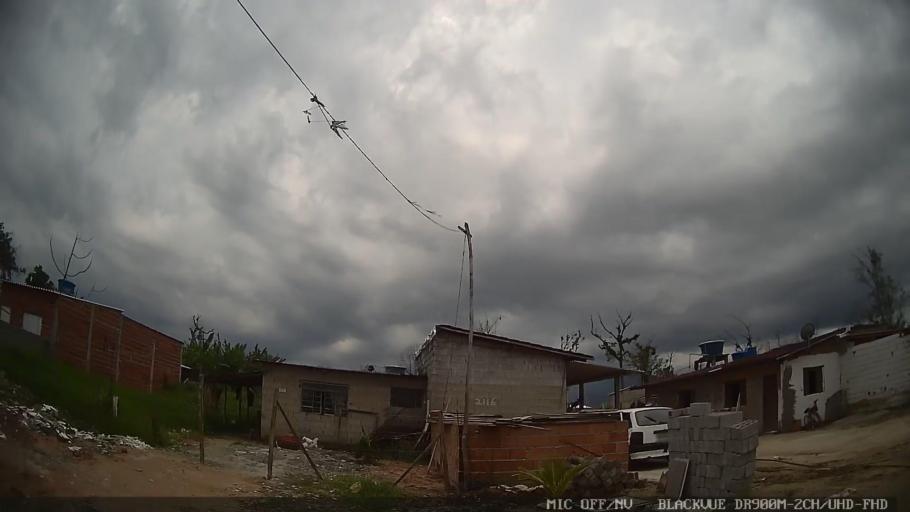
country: BR
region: Sao Paulo
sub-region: Caraguatatuba
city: Caraguatatuba
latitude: -23.6748
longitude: -45.4551
